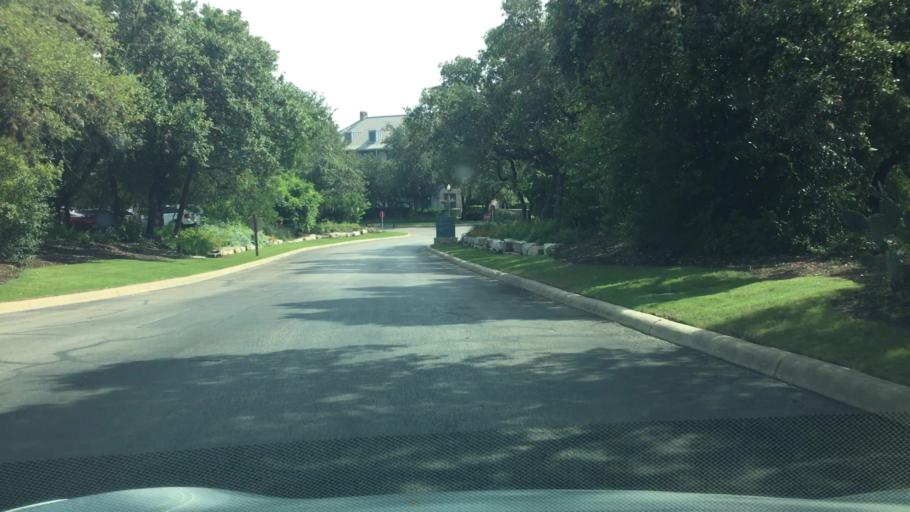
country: US
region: Texas
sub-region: Bexar County
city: Leon Valley
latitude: 29.4609
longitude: -98.6826
